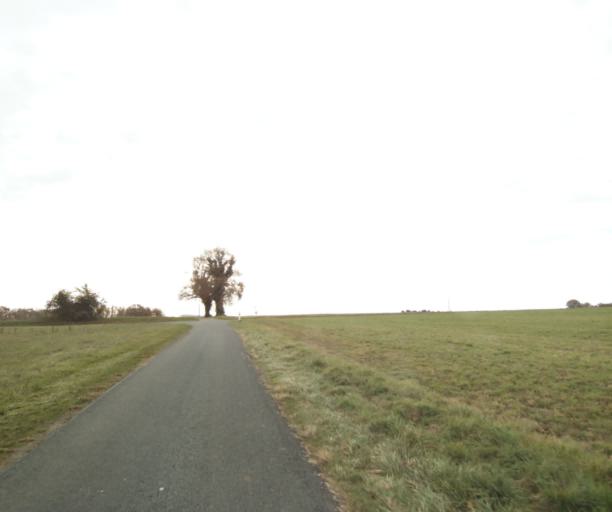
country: FR
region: Poitou-Charentes
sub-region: Departement de la Charente-Maritime
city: Corme-Royal
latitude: 45.7278
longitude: -0.7767
